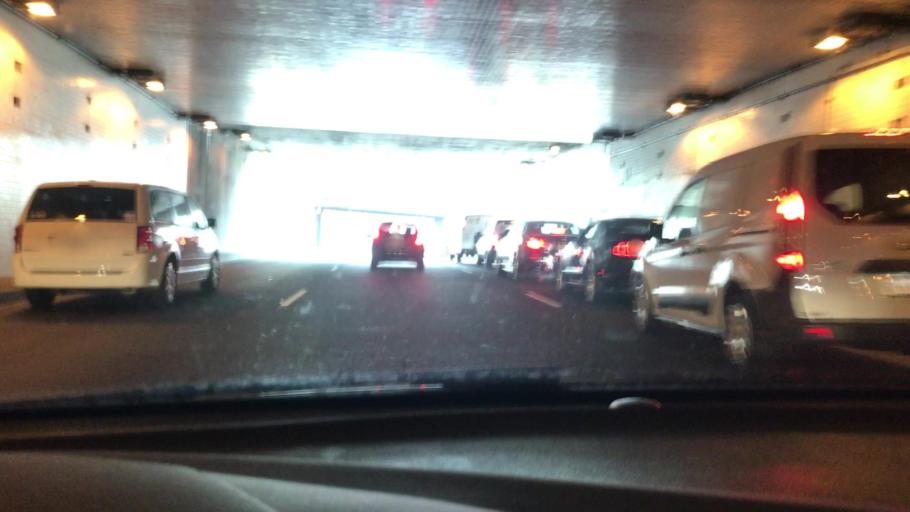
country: US
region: Washington, D.C.
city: Washington, D.C.
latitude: 38.8870
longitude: -77.0240
